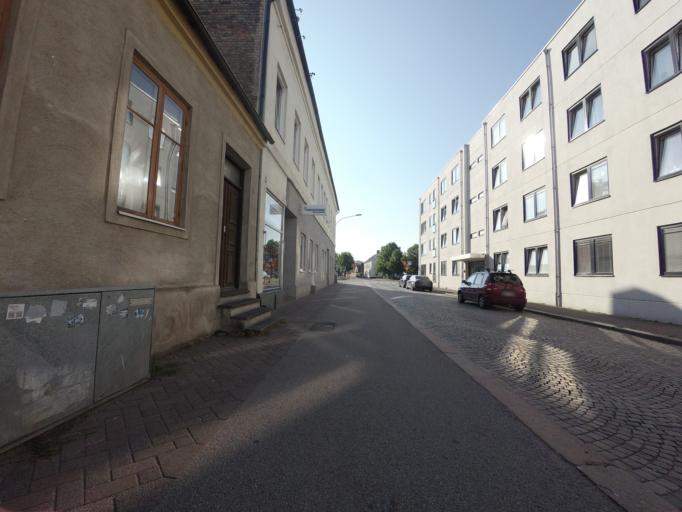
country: SE
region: Skane
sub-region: Trelleborgs Kommun
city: Trelleborg
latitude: 55.3716
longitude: 13.1657
